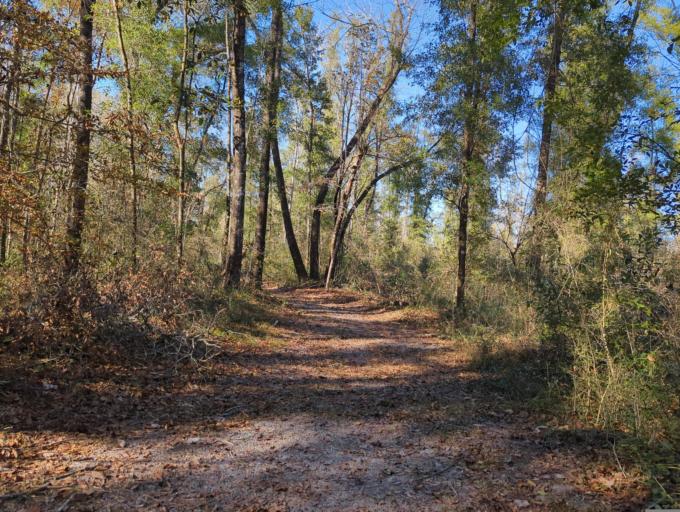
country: US
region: Florida
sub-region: Wakulla County
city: Crawfordville
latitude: 30.1851
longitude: -84.3259
